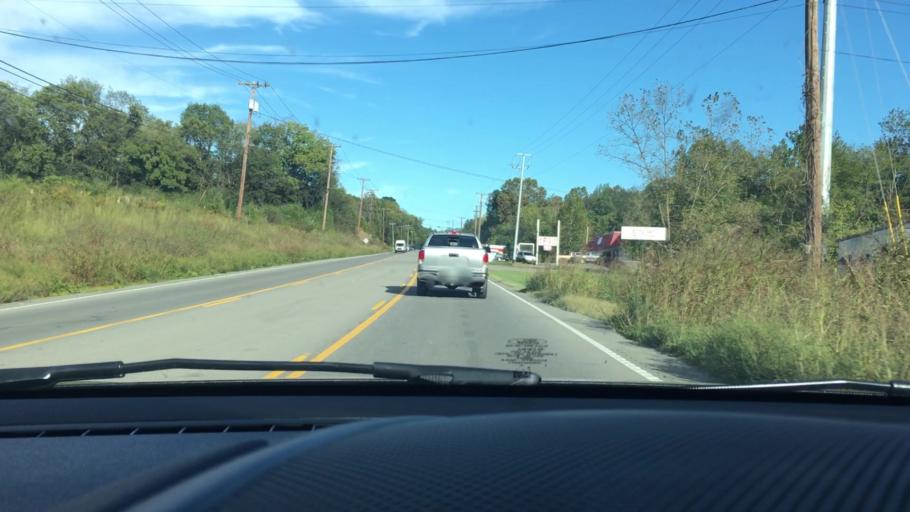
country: US
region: Tennessee
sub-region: Montgomery County
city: Clarksville
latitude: 36.5013
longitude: -87.3070
